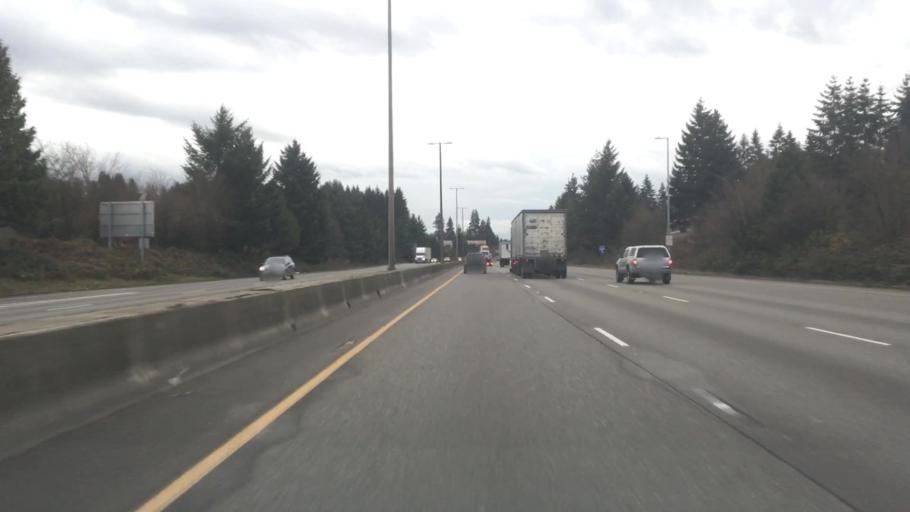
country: US
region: Washington
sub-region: Thurston County
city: Tumwater
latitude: 46.9976
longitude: -122.9136
